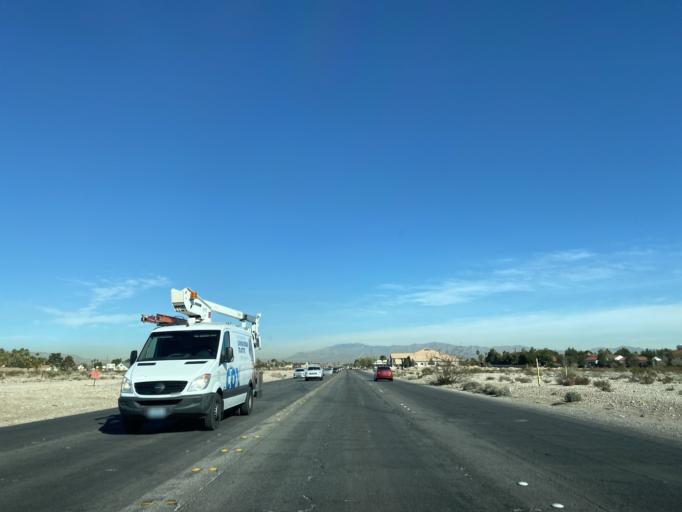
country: US
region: Nevada
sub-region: Clark County
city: Spring Valley
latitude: 36.0758
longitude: -115.2246
